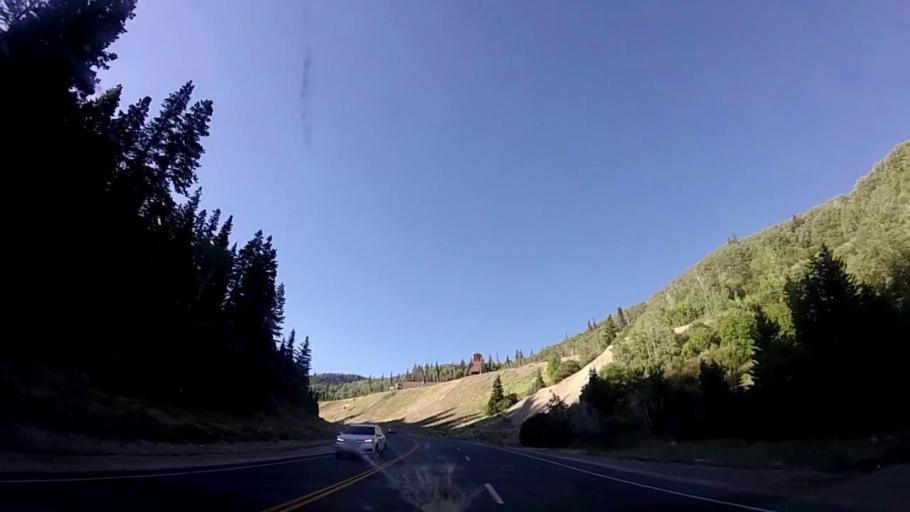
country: US
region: Utah
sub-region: Summit County
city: Park City
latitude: 40.6266
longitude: -111.4965
